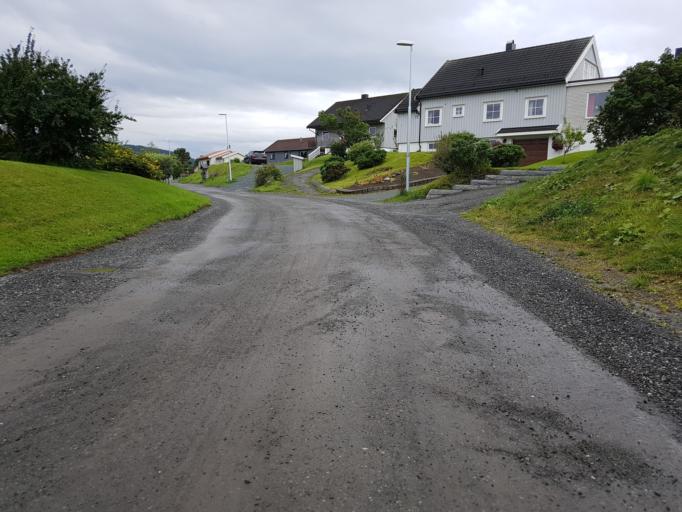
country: NO
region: Sor-Trondelag
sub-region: Trondheim
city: Trondheim
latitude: 63.3938
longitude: 10.4065
